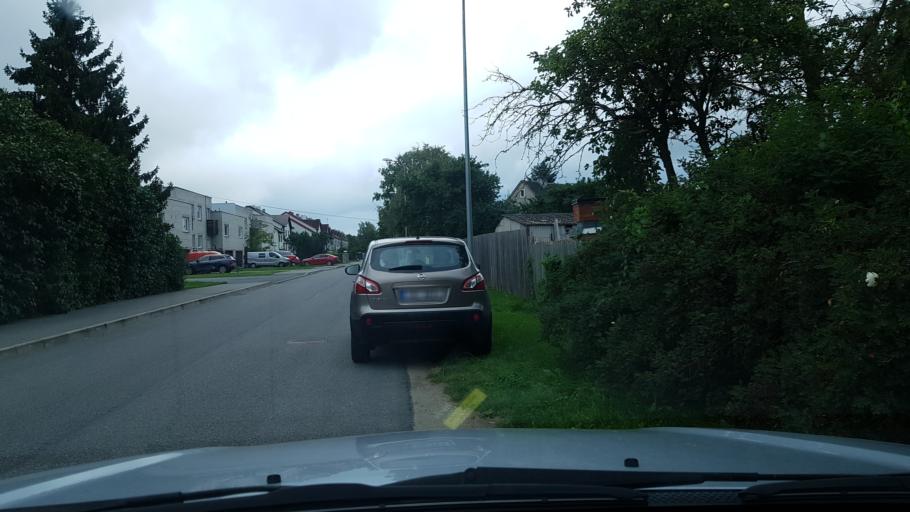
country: EE
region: Harju
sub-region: Tallinna linn
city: Tallinn
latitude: 59.4058
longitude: 24.8155
